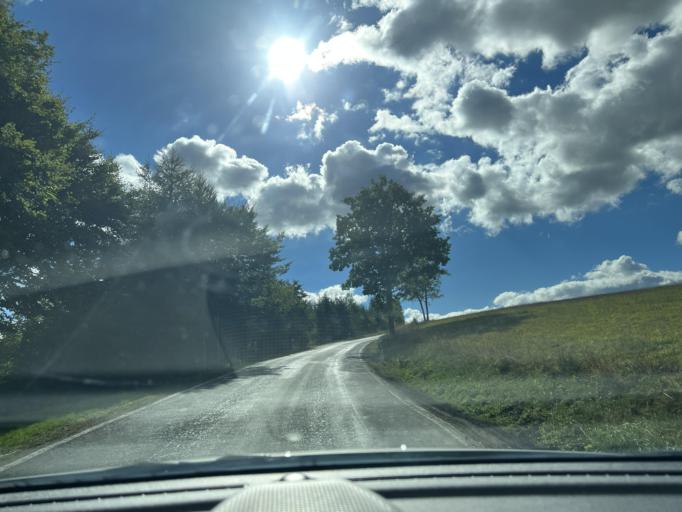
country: DE
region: North Rhine-Westphalia
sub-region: Regierungsbezirk Arnsberg
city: Erndtebruck
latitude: 50.9987
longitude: 8.3371
